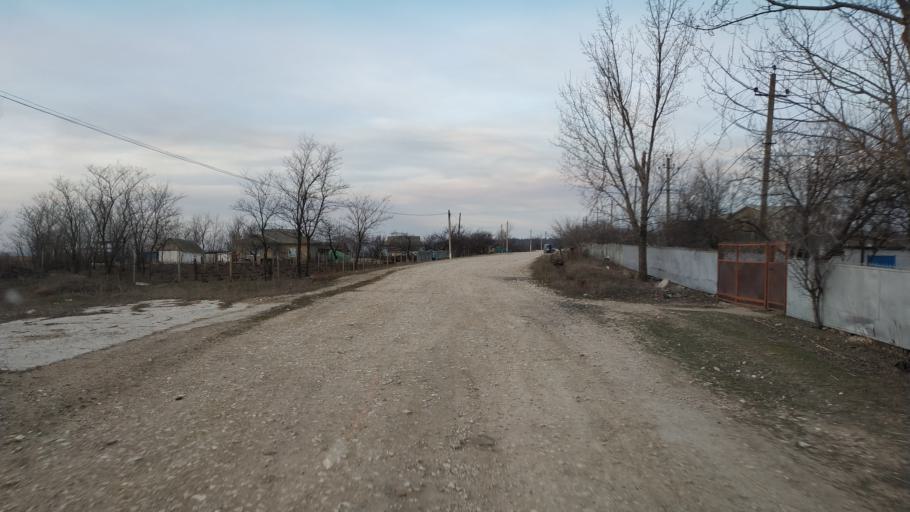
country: MD
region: Hincesti
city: Dancu
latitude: 46.7476
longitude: 28.2091
